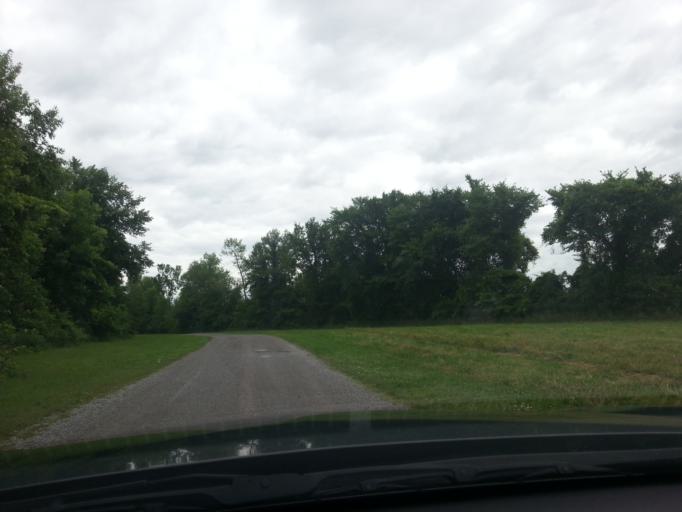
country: CA
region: Ontario
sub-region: Lanark County
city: Smiths Falls
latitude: 44.8913
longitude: -76.0573
